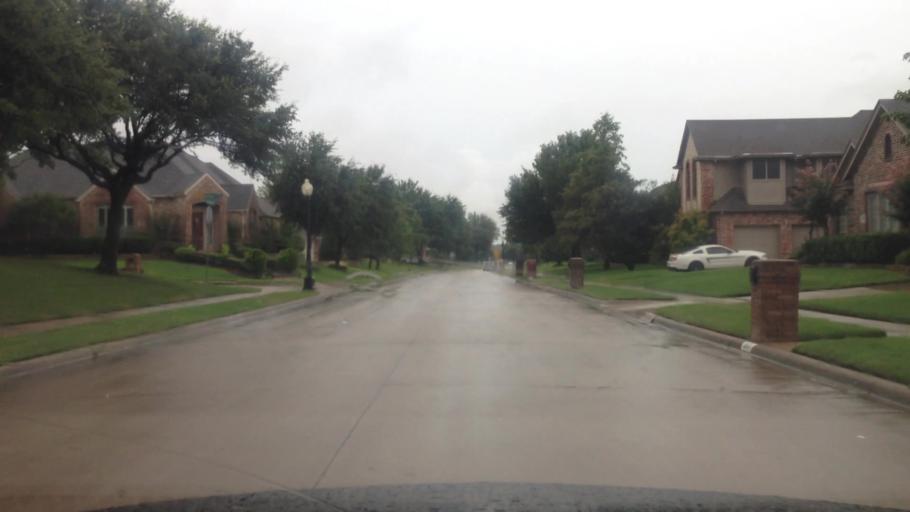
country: US
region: Texas
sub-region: Tarrant County
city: Keller
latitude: 32.9059
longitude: -97.2114
